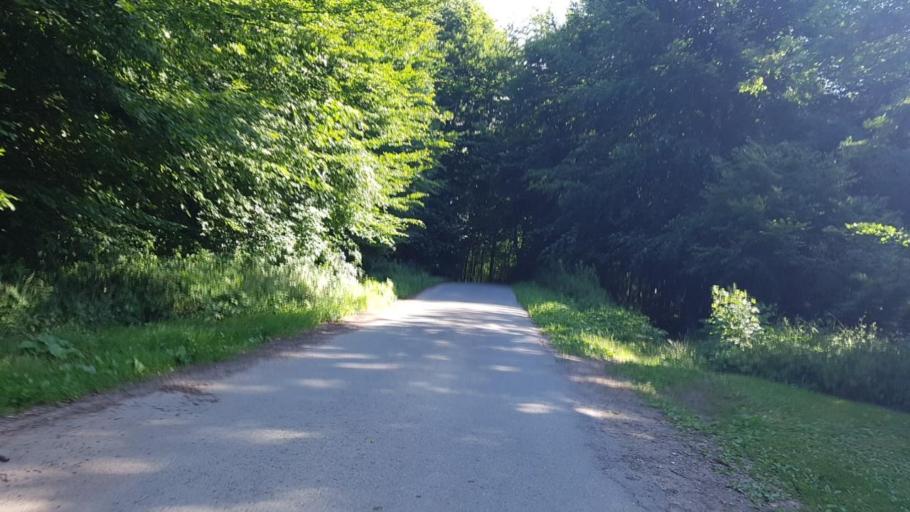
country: FR
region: Picardie
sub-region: Departement de l'Oise
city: Fleurines
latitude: 49.2565
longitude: 2.6196
